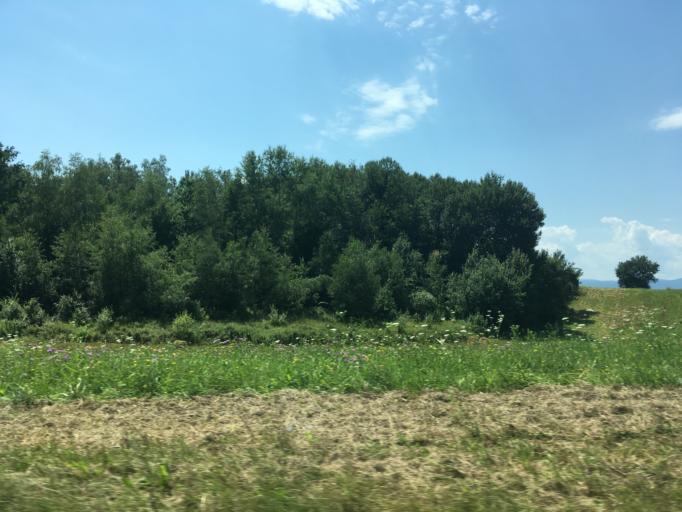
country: SI
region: Metlika
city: Metlika
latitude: 45.5985
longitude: 15.3403
